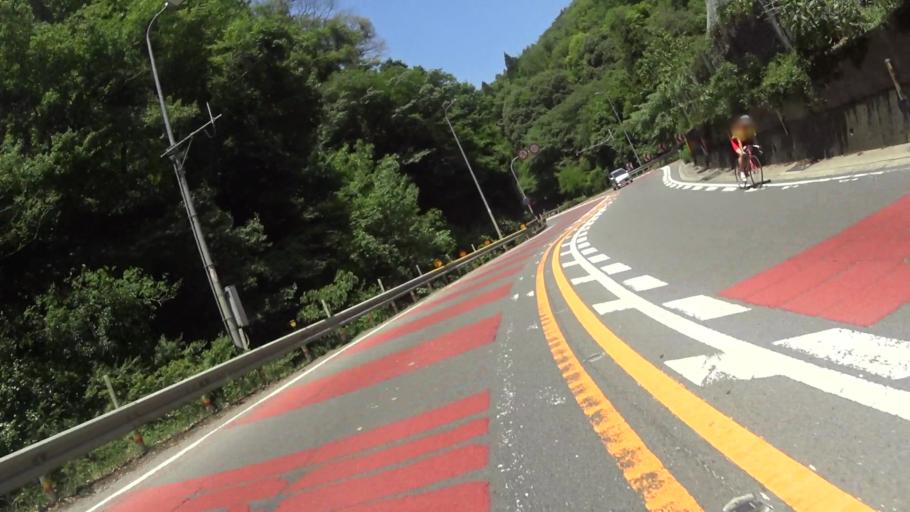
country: JP
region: Kyoto
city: Muko
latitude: 34.9906
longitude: 135.6523
